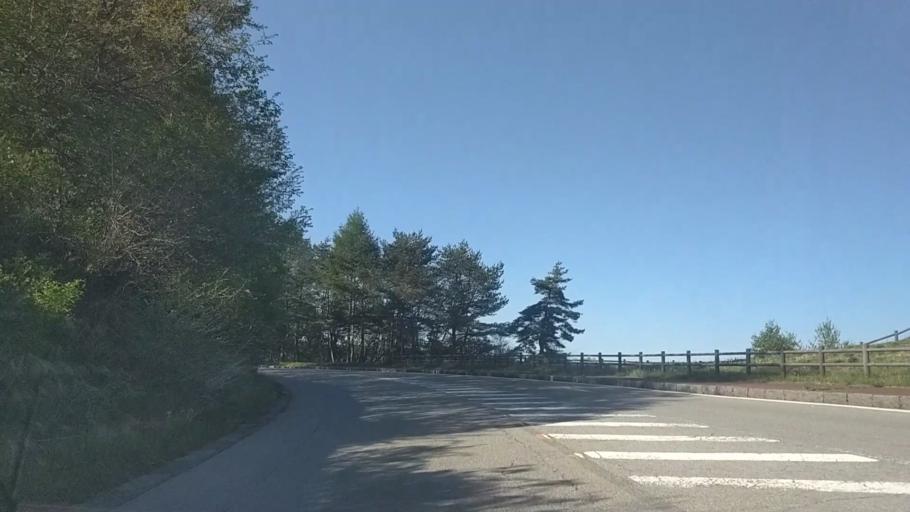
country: JP
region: Yamanashi
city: Nirasaki
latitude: 35.9234
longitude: 138.4077
